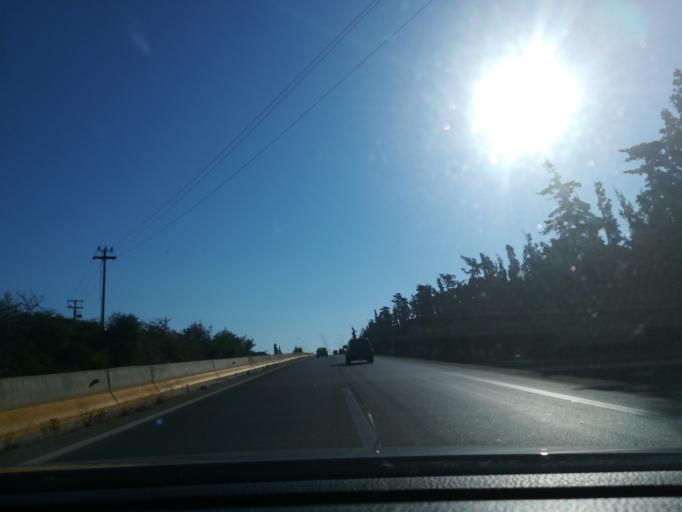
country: GR
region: Crete
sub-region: Nomos Irakleiou
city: Gournes
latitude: 35.3240
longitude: 25.2820
